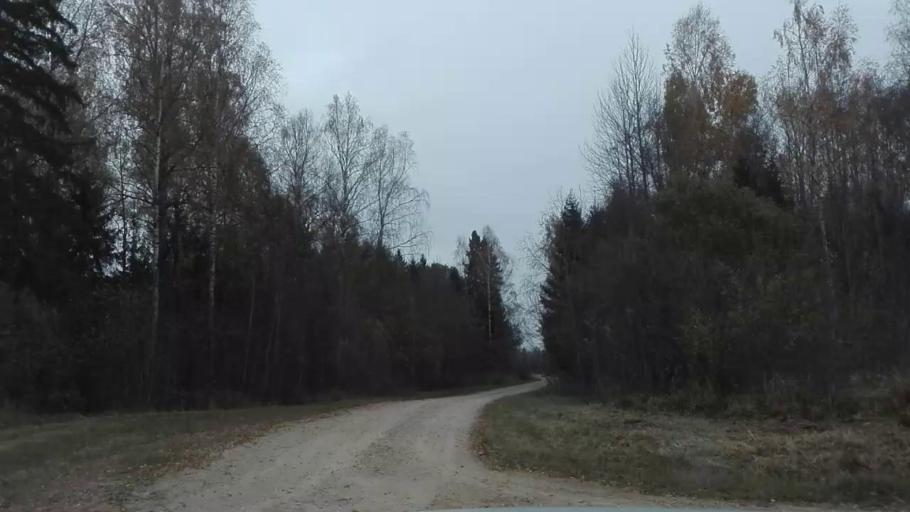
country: EE
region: Jogevamaa
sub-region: Poltsamaa linn
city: Poltsamaa
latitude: 58.5001
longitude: 25.9656
